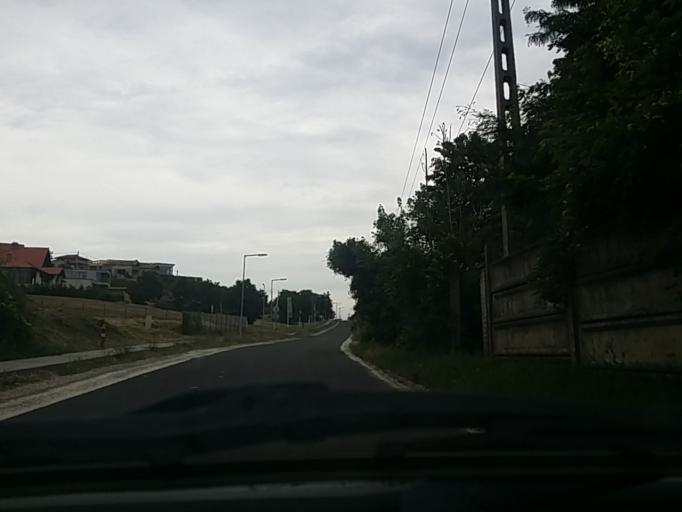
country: HU
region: Pest
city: Urom
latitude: 47.5938
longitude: 19.0256
